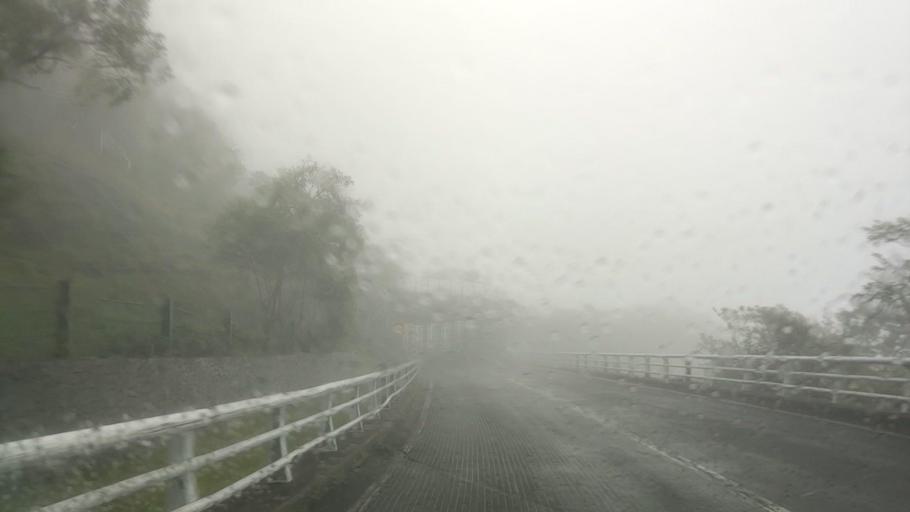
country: JP
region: Hokkaido
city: Date
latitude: 42.5494
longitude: 141.0851
